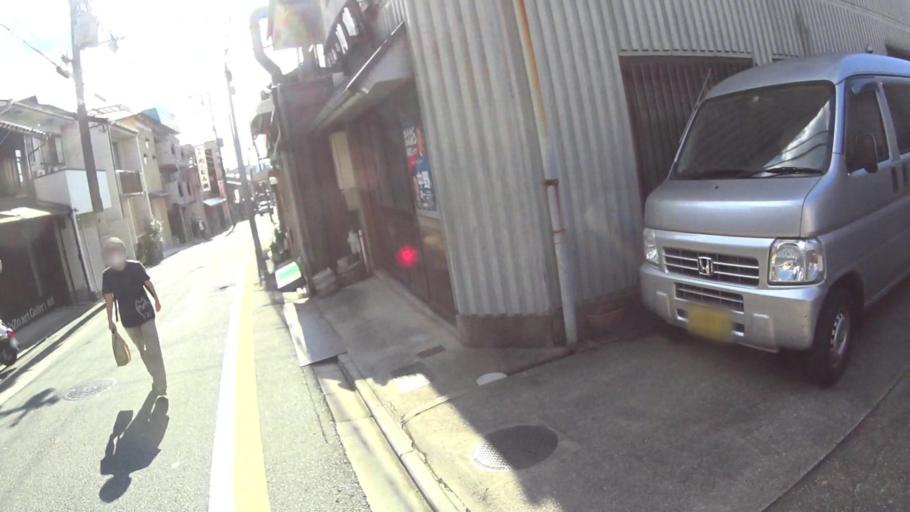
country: RU
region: Rostov
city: Remontnoye
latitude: 46.5012
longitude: 43.7601
